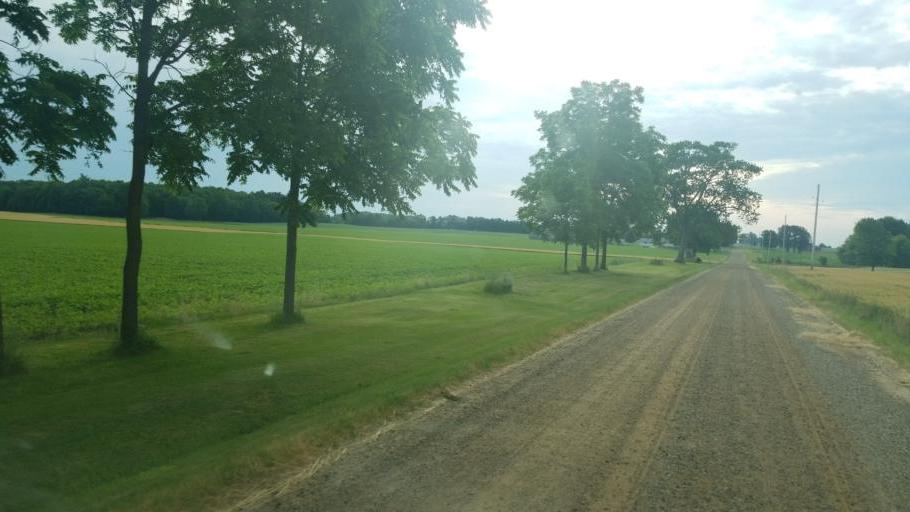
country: US
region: Michigan
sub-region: Eaton County
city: Charlotte
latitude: 42.6118
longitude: -84.9367
